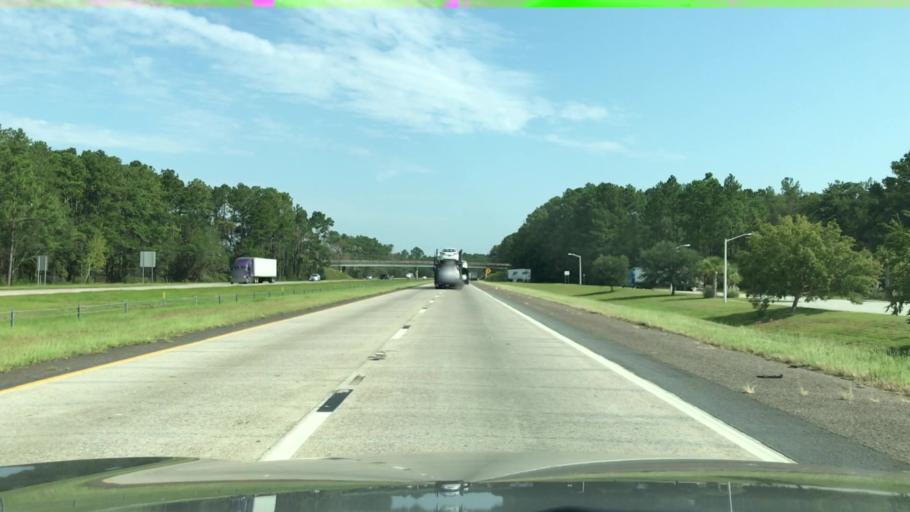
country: US
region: South Carolina
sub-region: Hampton County
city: Yemassee
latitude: 32.8023
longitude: -80.7708
